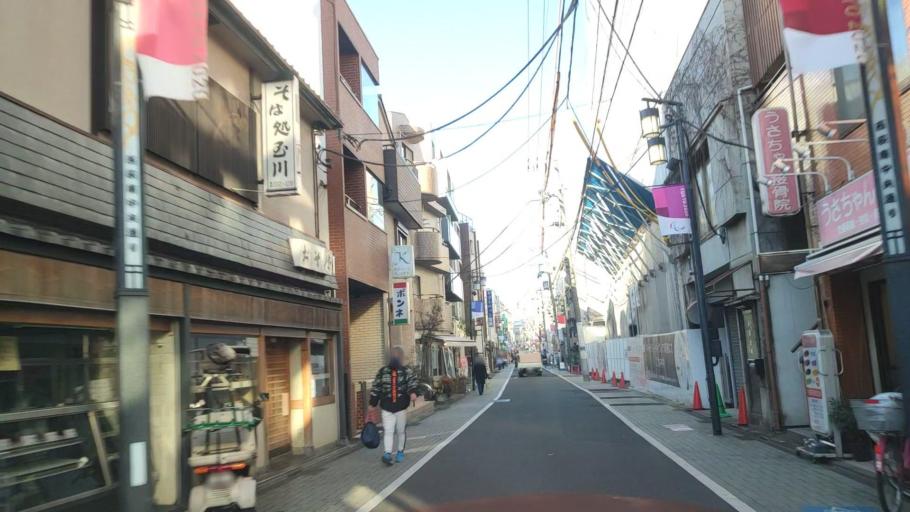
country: JP
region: Tokyo
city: Musashino
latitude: 35.6999
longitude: 139.5988
